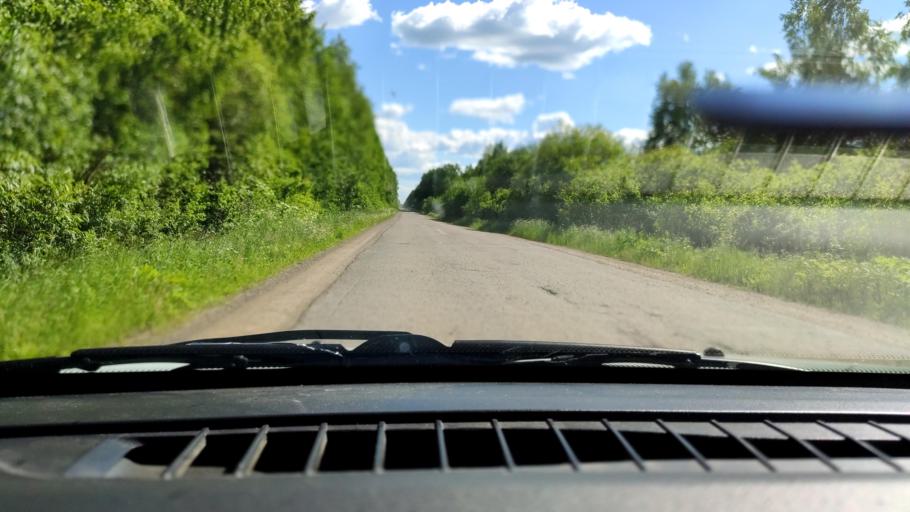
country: RU
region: Perm
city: Kukushtan
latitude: 57.2743
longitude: 56.5348
